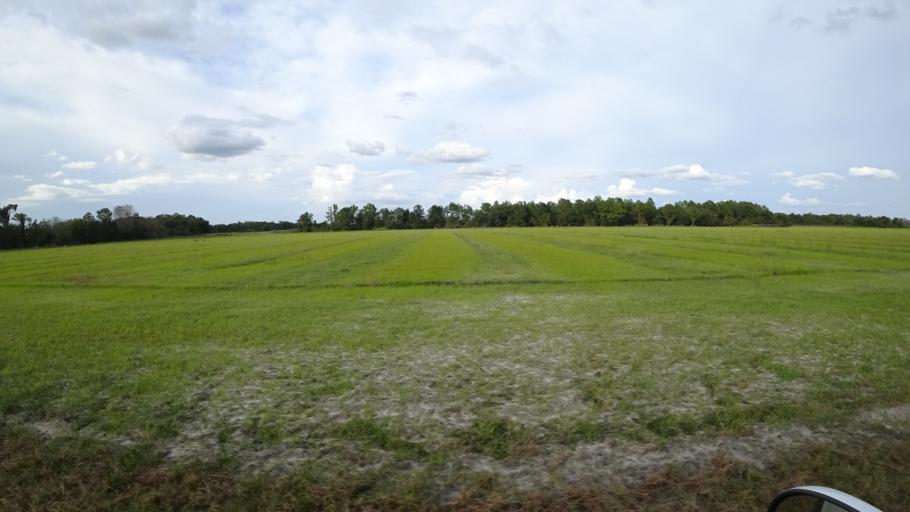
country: US
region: Florida
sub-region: Hillsborough County
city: Wimauma
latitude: 27.5591
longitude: -82.0808
